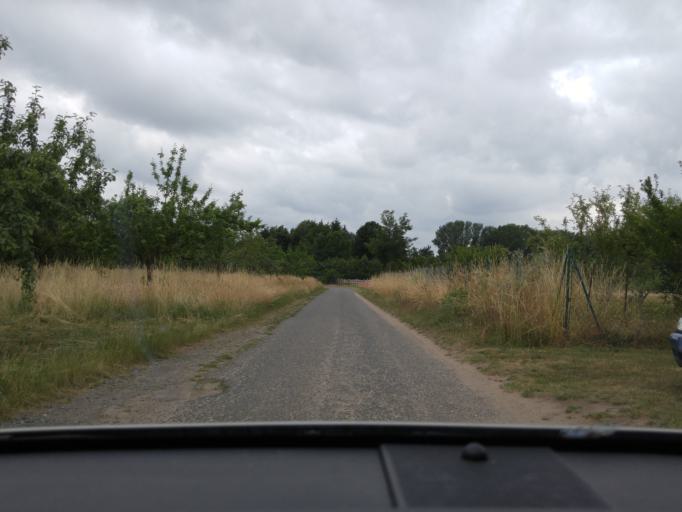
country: DE
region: Hesse
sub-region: Regierungsbezirk Darmstadt
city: Egelsbach
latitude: 49.9666
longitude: 8.6837
